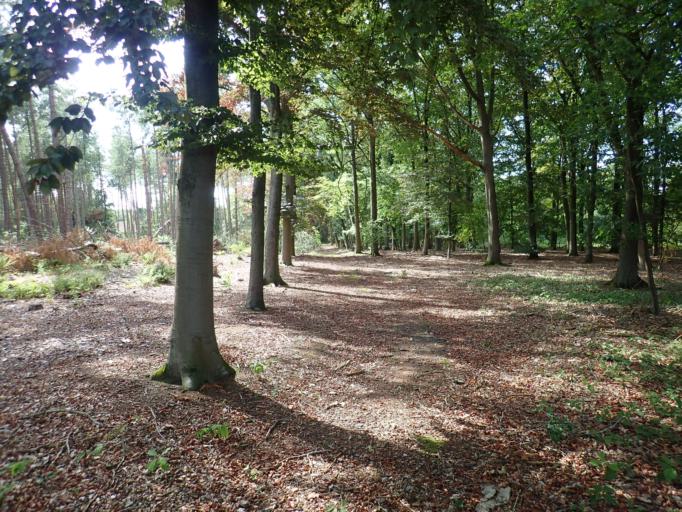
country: BE
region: Flanders
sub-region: Provincie Antwerpen
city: Beerse
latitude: 51.3013
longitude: 4.8087
